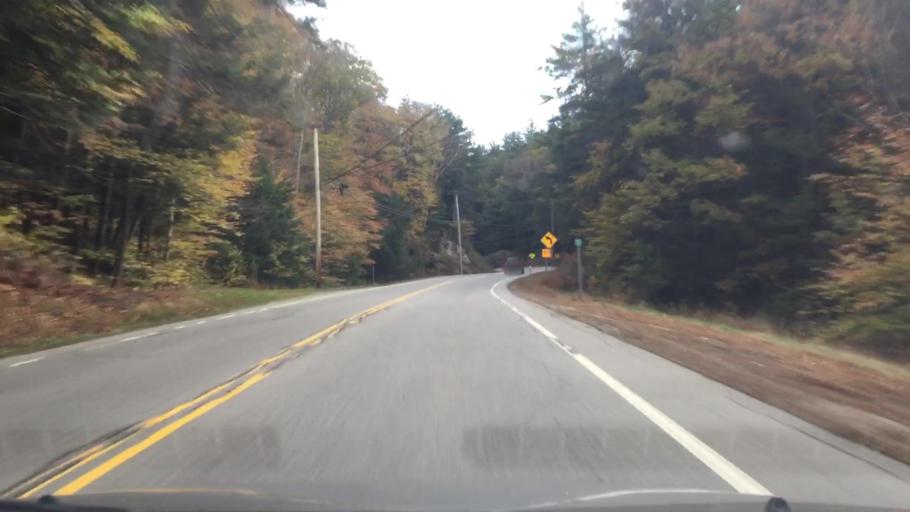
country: US
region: New Hampshire
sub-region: Cheshire County
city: Keene
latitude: 43.0255
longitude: -72.2683
